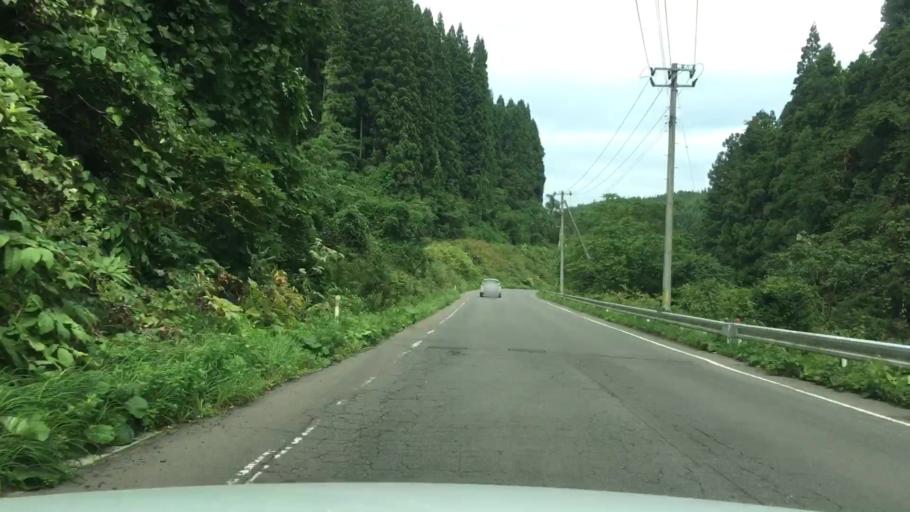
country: JP
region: Aomori
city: Shimokizukuri
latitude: 40.7392
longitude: 140.2453
